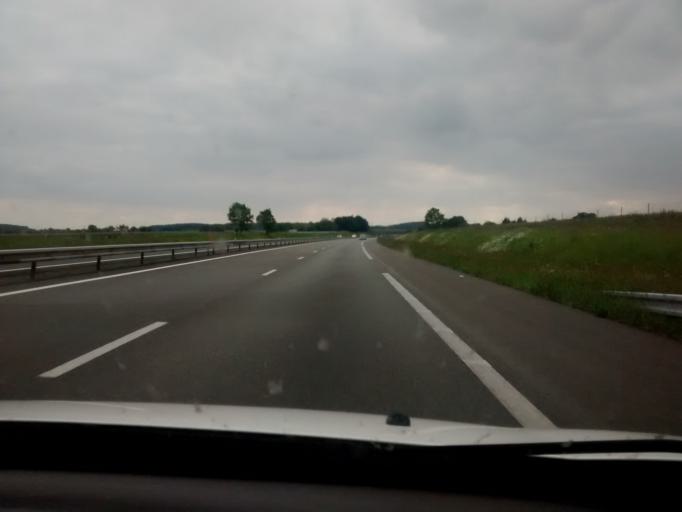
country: FR
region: Pays de la Loire
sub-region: Departement de la Sarthe
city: Louplande
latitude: 48.0143
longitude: -0.0672
